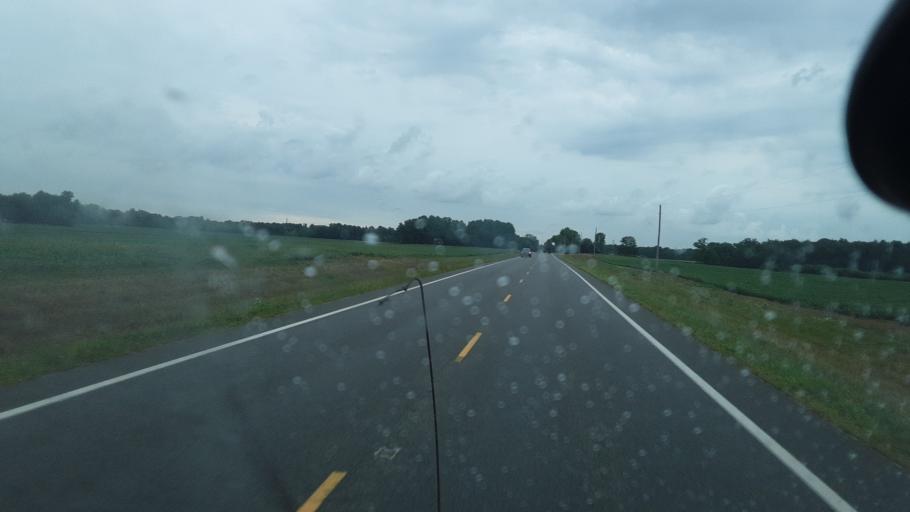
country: US
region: Ohio
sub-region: Williams County
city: Bryan
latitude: 41.4088
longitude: -84.6290
